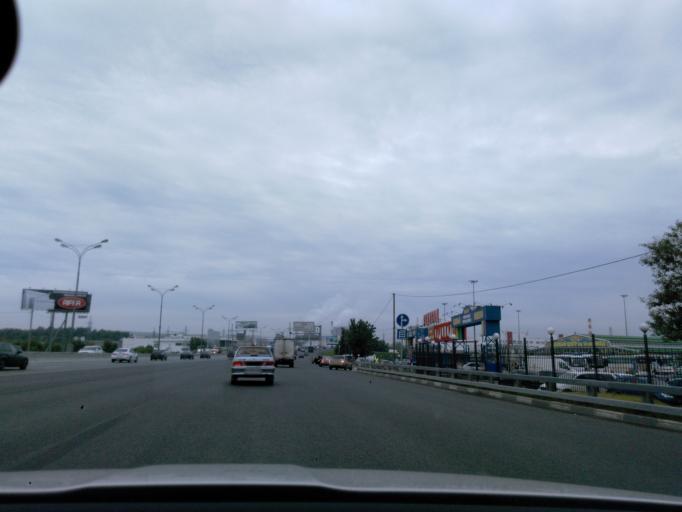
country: RU
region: Moskovskaya
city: Kotel'niki
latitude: 55.6540
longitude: 37.8373
